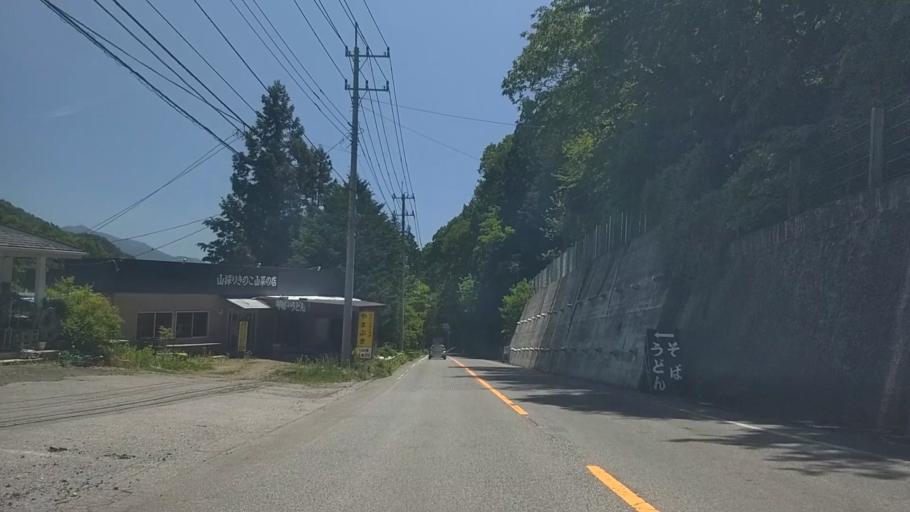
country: JP
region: Yamanashi
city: Nirasaki
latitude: 35.8821
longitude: 138.4264
